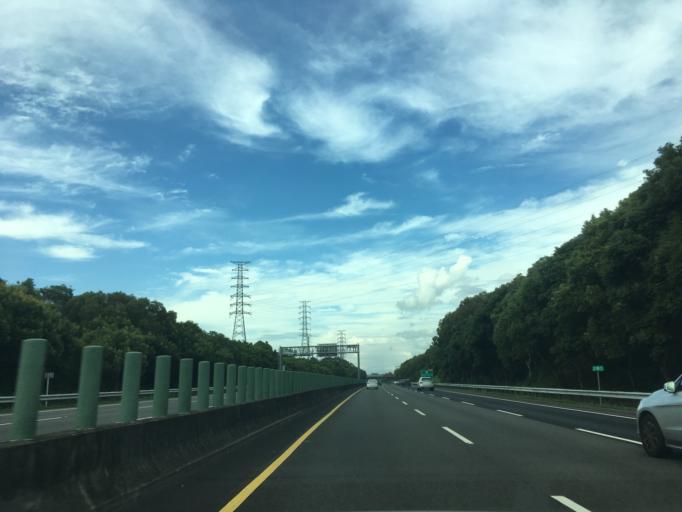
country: TW
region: Taiwan
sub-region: Chiayi
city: Jiayi Shi
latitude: 23.5833
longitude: 120.5125
